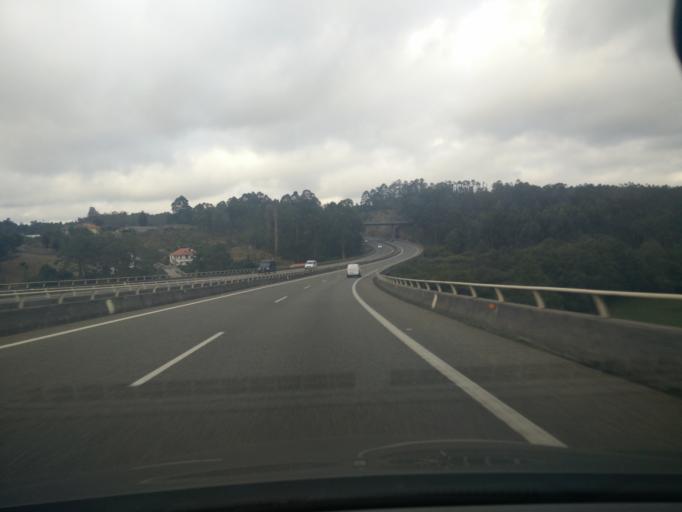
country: ES
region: Galicia
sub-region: Provincia da Coruna
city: Arteixo
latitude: 43.2906
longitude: -8.4949
